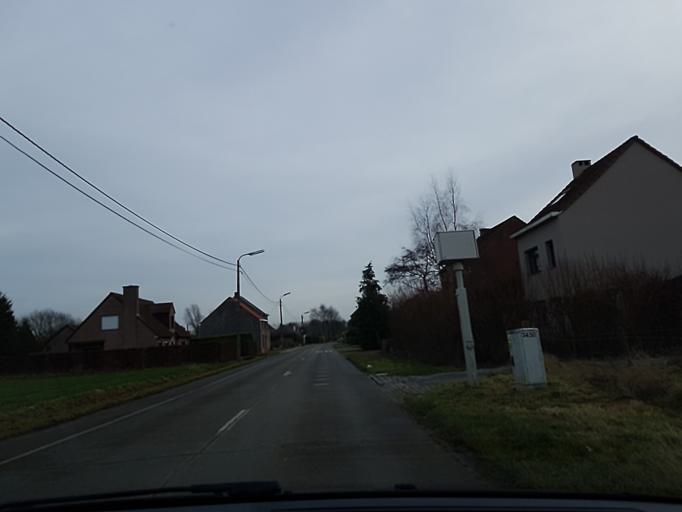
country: BE
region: Flanders
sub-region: Provincie Vlaams-Brabant
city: Boortmeerbeek
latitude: 51.0021
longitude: 4.5765
